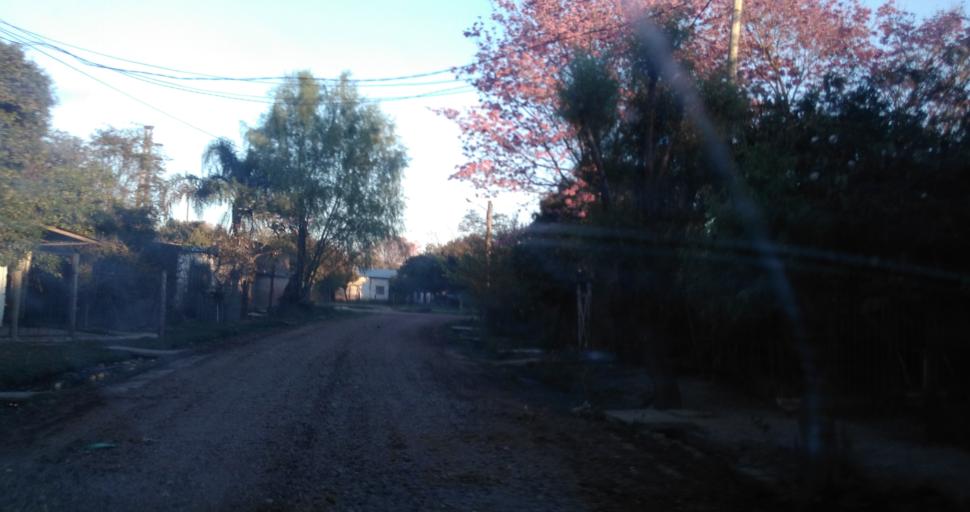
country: AR
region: Chaco
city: Fontana
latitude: -27.4285
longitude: -59.0195
